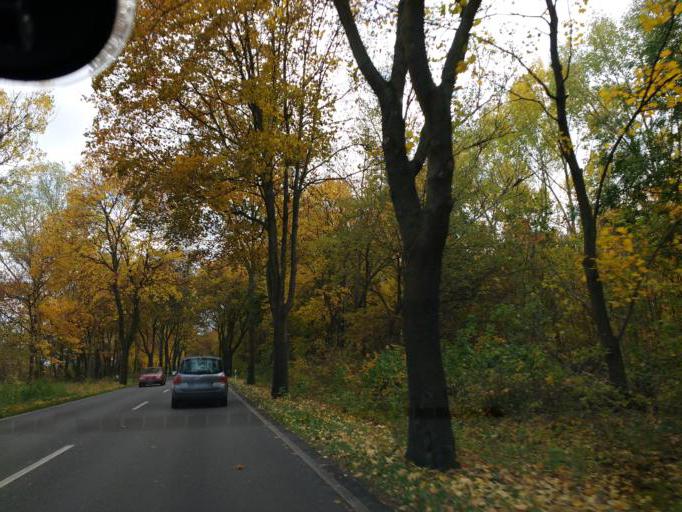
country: DE
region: Berlin
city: Hellersdorf
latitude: 52.5455
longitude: 13.6118
